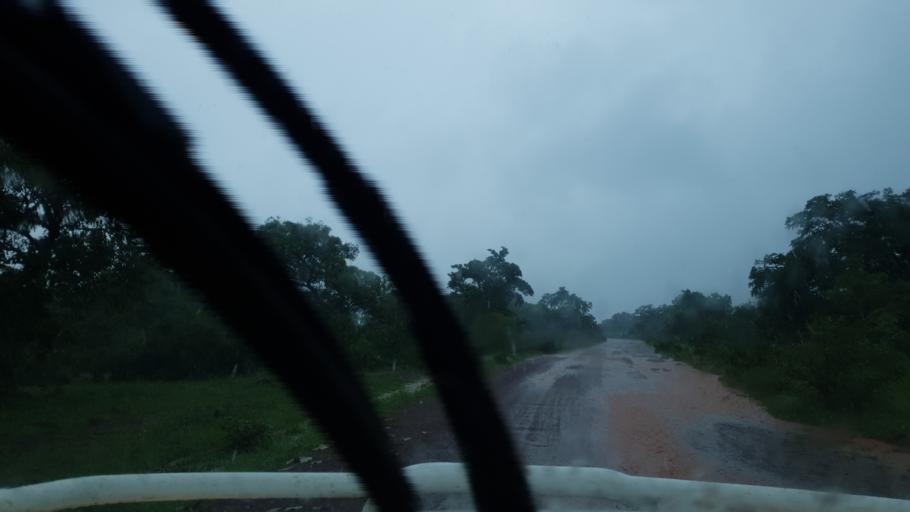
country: ML
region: Sikasso
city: Kolondieba
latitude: 11.6129
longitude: -6.6761
